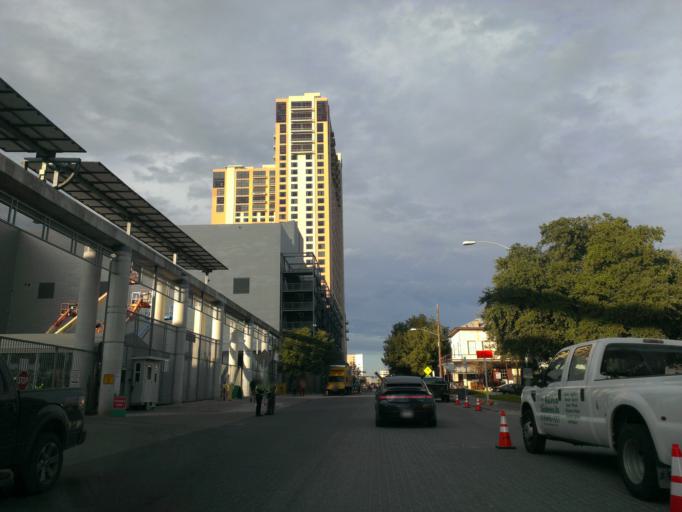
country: US
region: Texas
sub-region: Travis County
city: Austin
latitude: 30.2631
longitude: -97.7384
